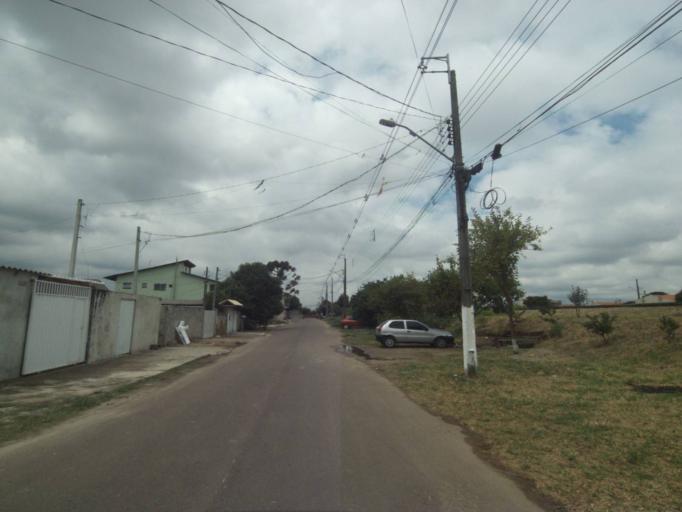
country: BR
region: Parana
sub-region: Pinhais
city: Pinhais
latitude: -25.4576
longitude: -49.1995
